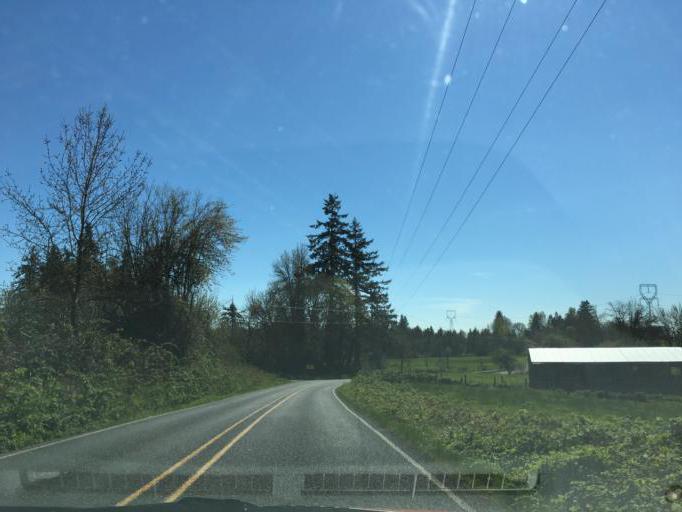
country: US
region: Oregon
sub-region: Marion County
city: Hubbard
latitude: 45.1543
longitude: -122.7228
